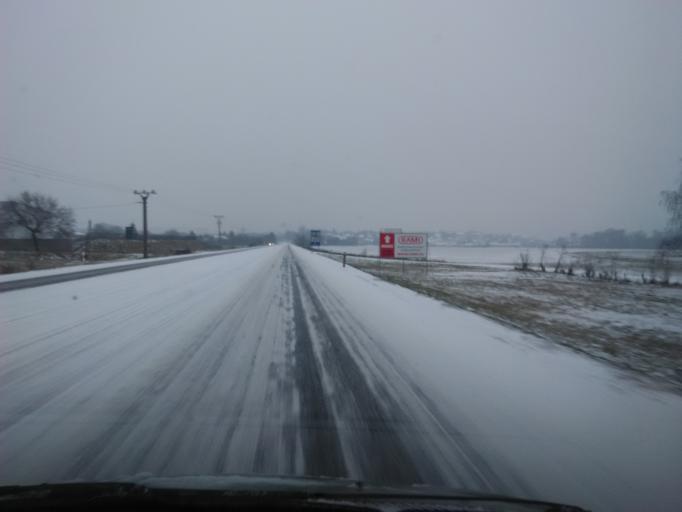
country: CZ
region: Olomoucky
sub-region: Okres Prerov
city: Hranice
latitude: 49.5488
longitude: 17.7039
